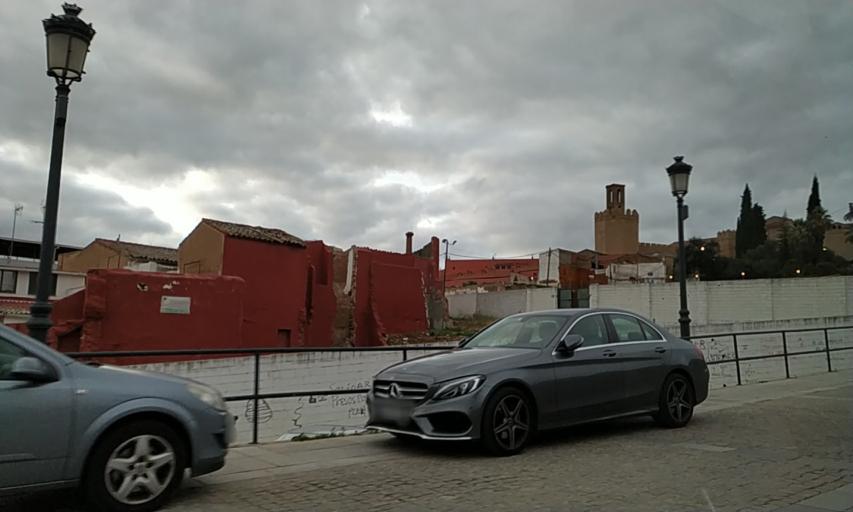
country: ES
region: Extremadura
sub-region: Provincia de Badajoz
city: Badajoz
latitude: 38.8802
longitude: -6.9656
